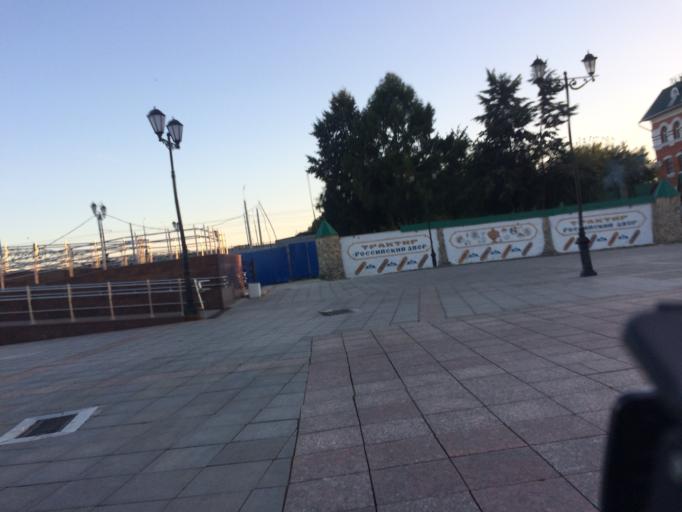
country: RU
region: Mariy-El
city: Yoshkar-Ola
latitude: 56.6297
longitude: 47.8993
